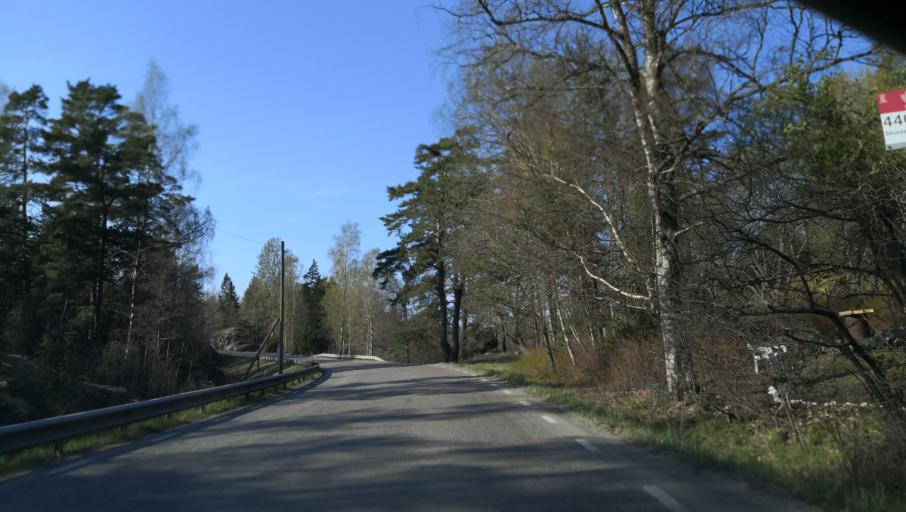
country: SE
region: Stockholm
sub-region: Varmdo Kommun
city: Holo
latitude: 59.3076
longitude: 18.5861
